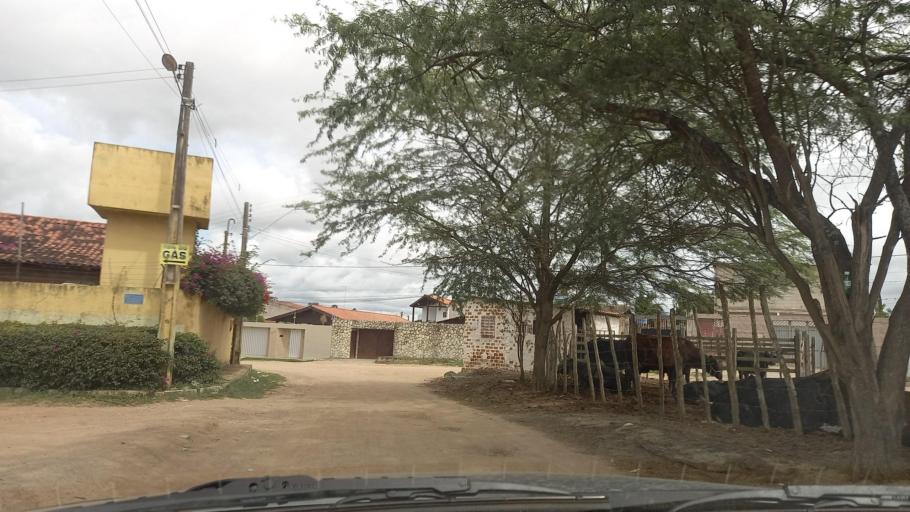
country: ET
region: Oromiya
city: Gore
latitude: 8.1937
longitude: 35.5772
